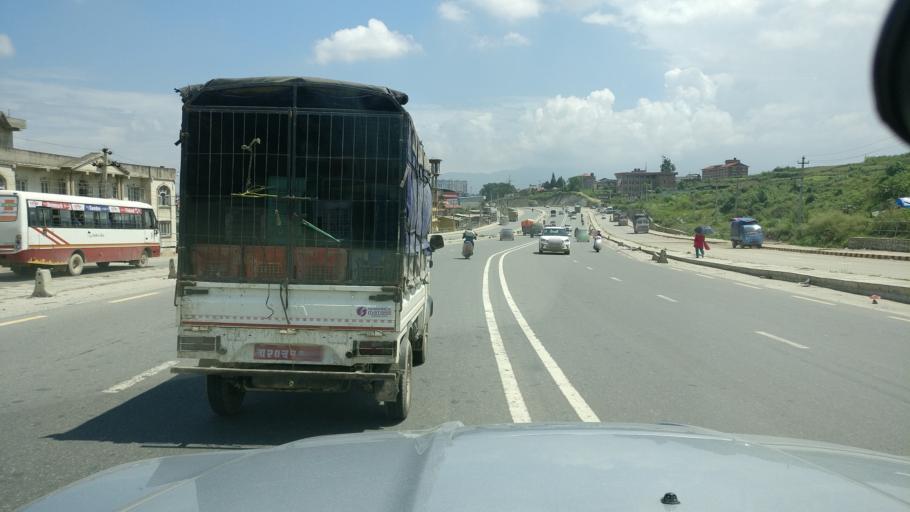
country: NP
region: Central Region
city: Kirtipur
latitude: 27.6877
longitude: 85.2904
